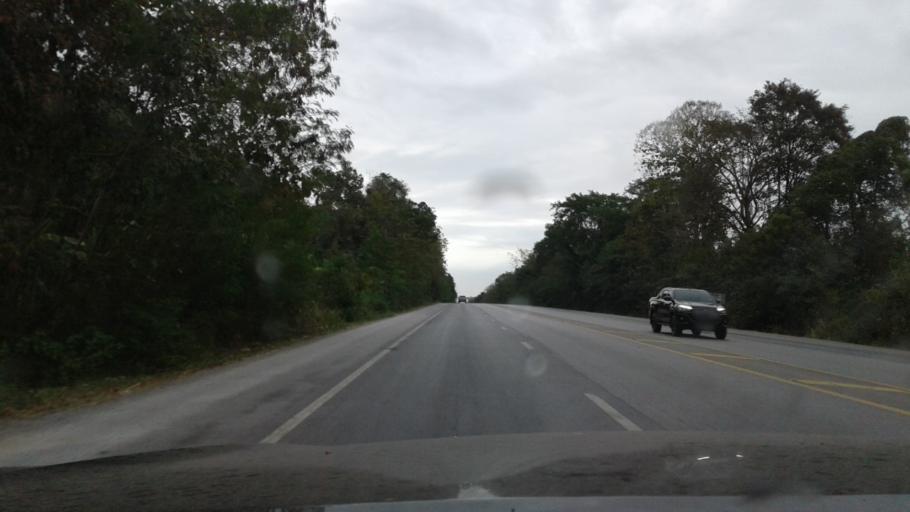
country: TH
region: Changwat Udon Thani
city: Nong Wua So
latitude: 17.2505
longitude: 102.5682
